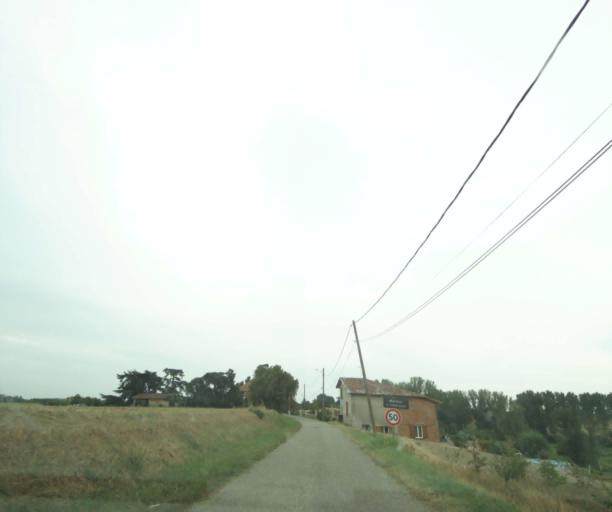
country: FR
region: Midi-Pyrenees
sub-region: Departement du Tarn-et-Garonne
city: Saint-Porquier
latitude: 43.9753
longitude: 1.1847
